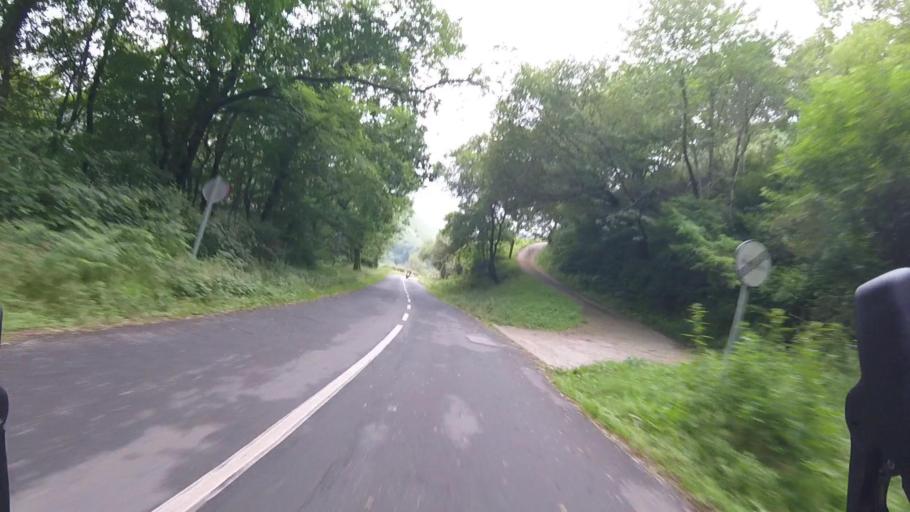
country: ES
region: Basque Country
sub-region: Provincia de Guipuzcoa
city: Irun
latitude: 43.2723
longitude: -1.8097
